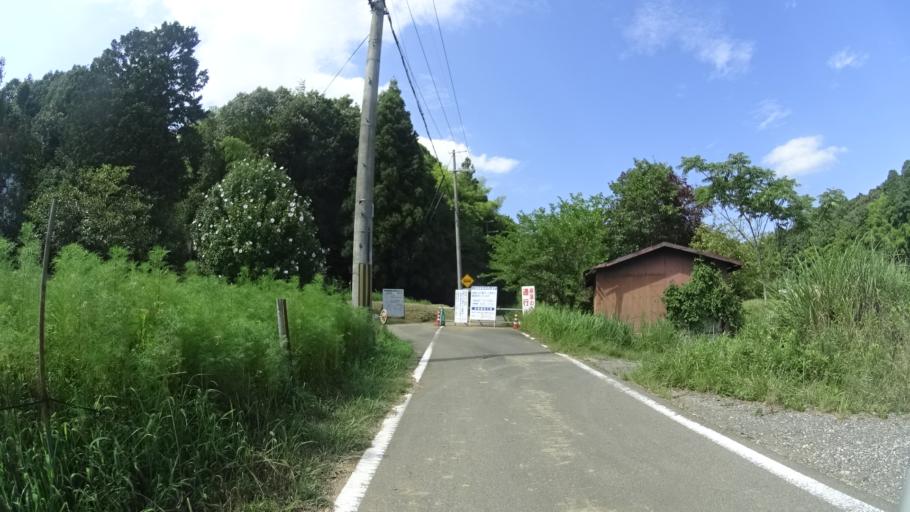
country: JP
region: Kyoto
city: Maizuru
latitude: 35.4340
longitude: 135.2963
